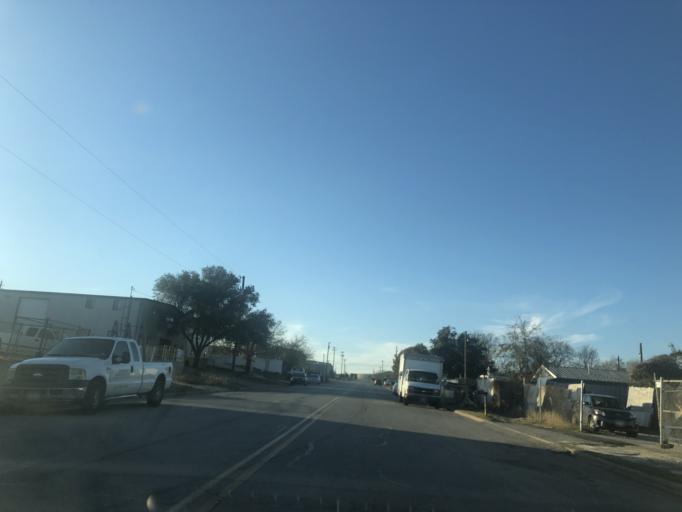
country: US
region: Texas
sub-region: Travis County
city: Wells Branch
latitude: 30.4306
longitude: -97.6776
